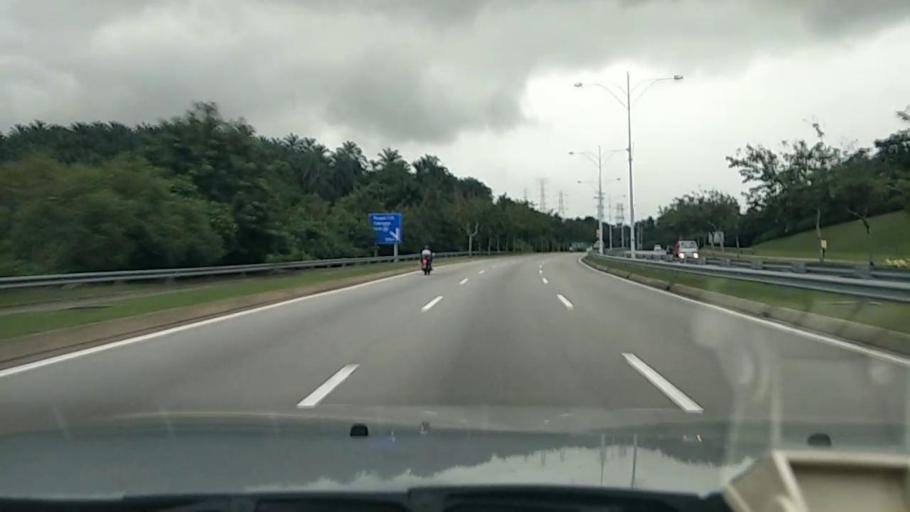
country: MY
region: Putrajaya
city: Putrajaya
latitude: 2.9495
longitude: 101.7133
